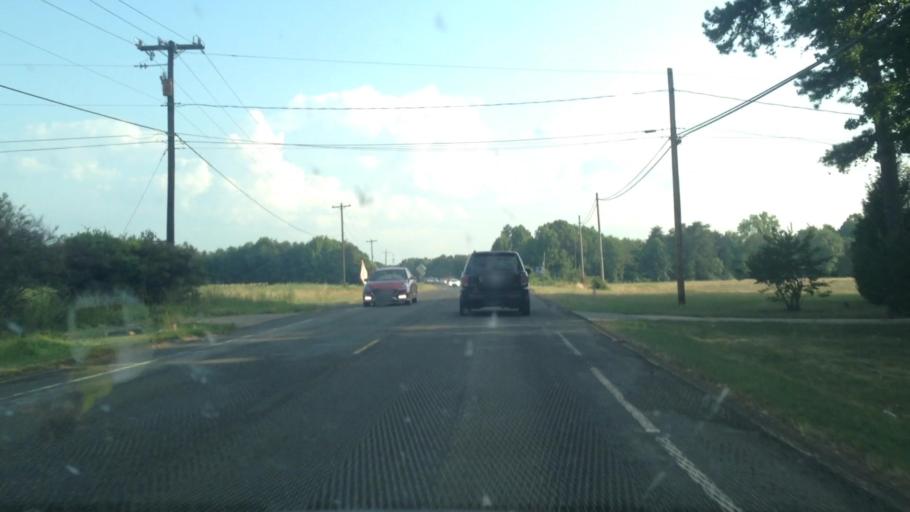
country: US
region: North Carolina
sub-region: Davidson County
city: Wallburg
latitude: 36.0308
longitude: -80.0566
